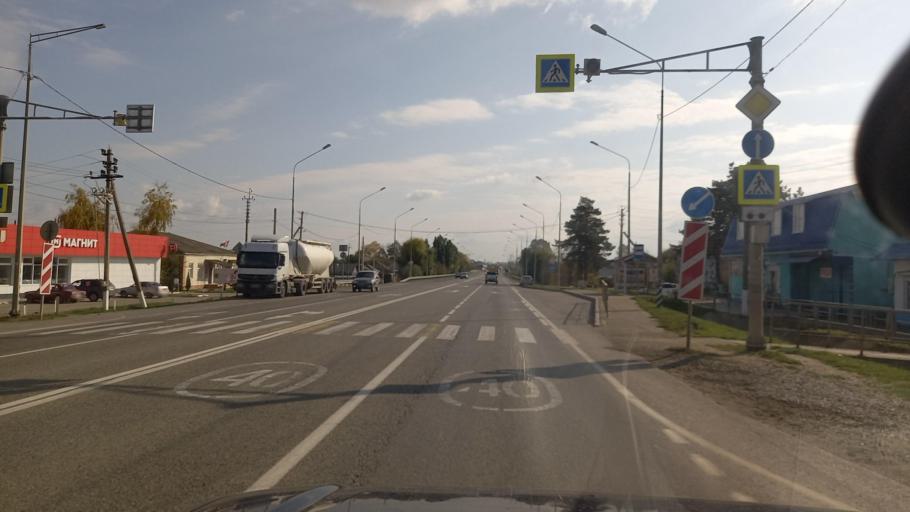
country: RU
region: Krasnodarskiy
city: Novoukrainskiy
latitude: 44.8958
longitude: 38.0536
